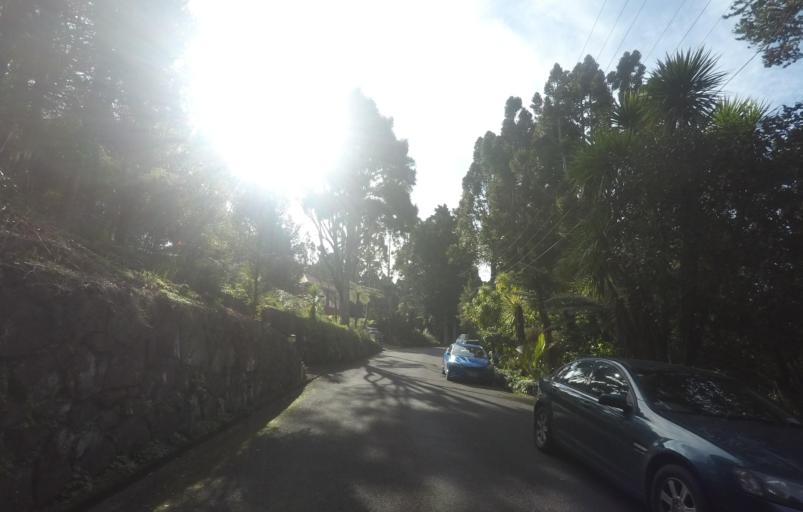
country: NZ
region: Auckland
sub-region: Auckland
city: Titirangi
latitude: -36.9409
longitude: 174.6427
